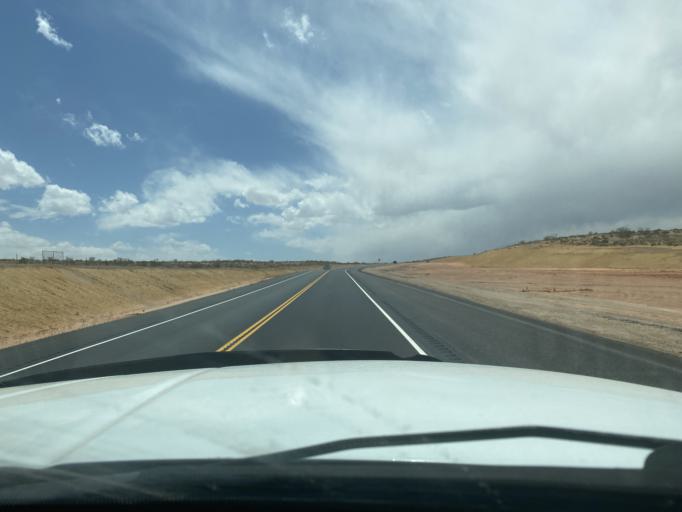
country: US
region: Utah
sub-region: Washington County
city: Hurricane
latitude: 37.1138
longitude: -113.3432
